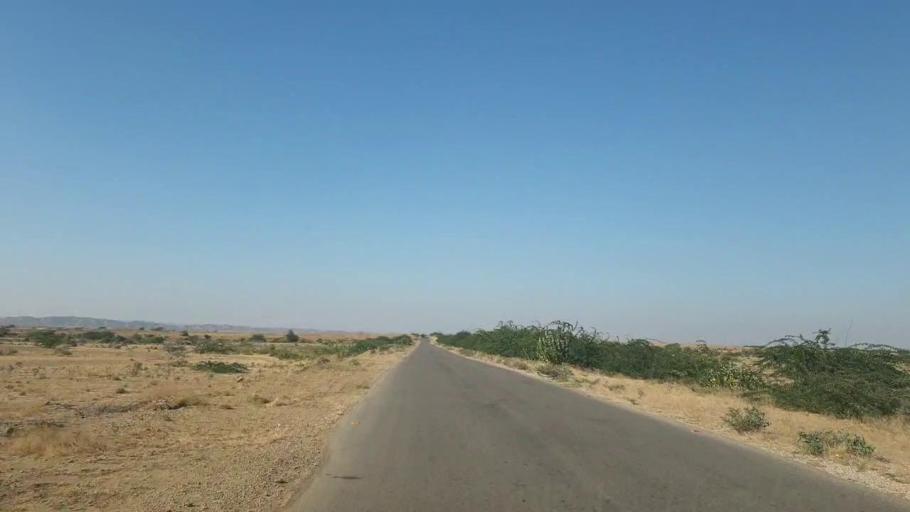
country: PK
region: Sindh
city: Malir Cantonment
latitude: 25.2625
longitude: 67.5984
